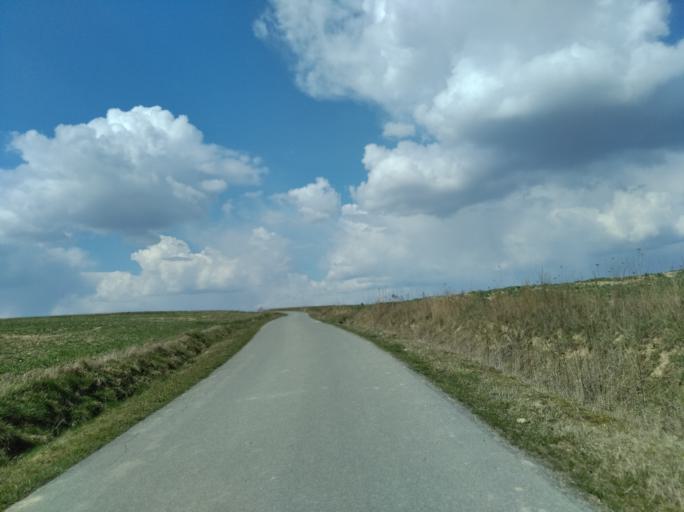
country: PL
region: Subcarpathian Voivodeship
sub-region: Powiat strzyzowski
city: Wisniowa
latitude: 49.9352
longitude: 21.7193
